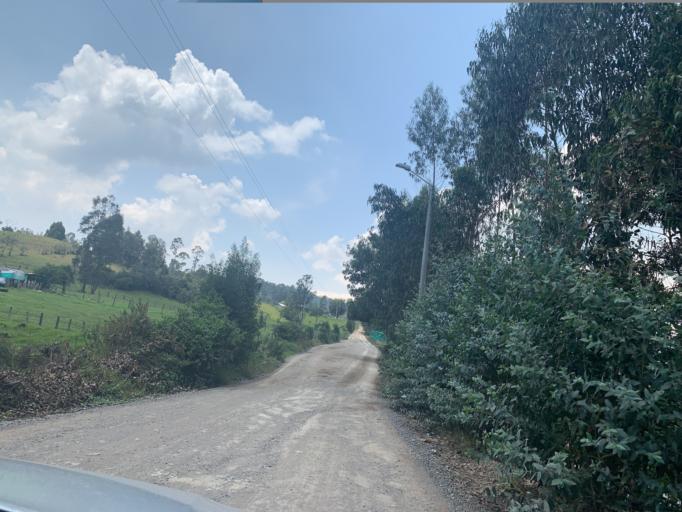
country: CO
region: Boyaca
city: Chiquinquira
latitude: 5.5990
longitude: -73.7628
